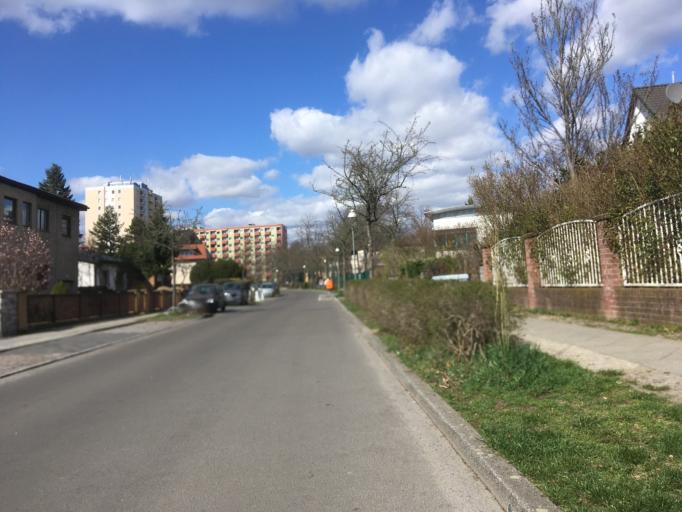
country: DE
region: Berlin
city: Lichtenrade
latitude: 52.4151
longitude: 13.4105
